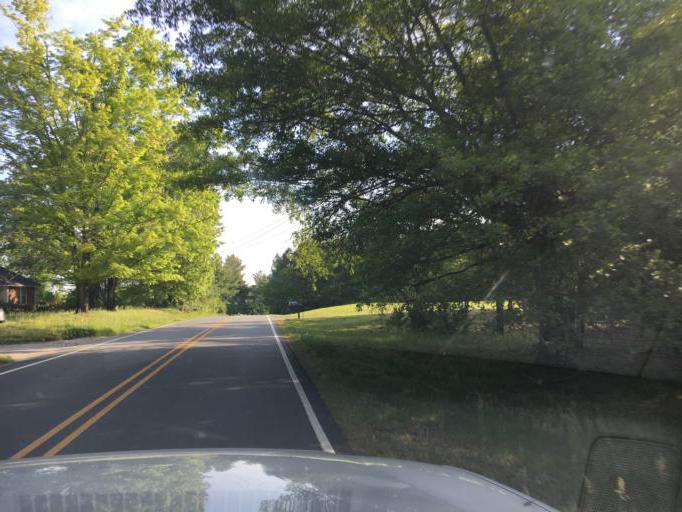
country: US
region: North Carolina
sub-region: Rutherford County
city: Rutherfordton
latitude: 35.3654
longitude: -81.9777
